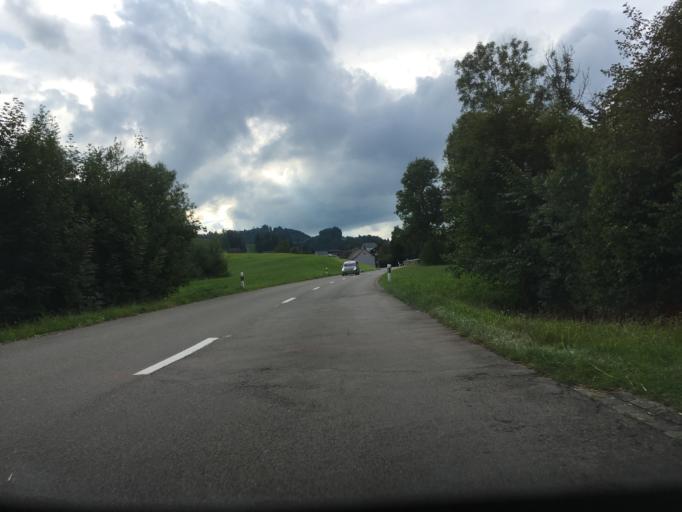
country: CH
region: Saint Gallen
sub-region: Wahlkreis Toggenburg
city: Mosnang
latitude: 47.3708
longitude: 8.9950
